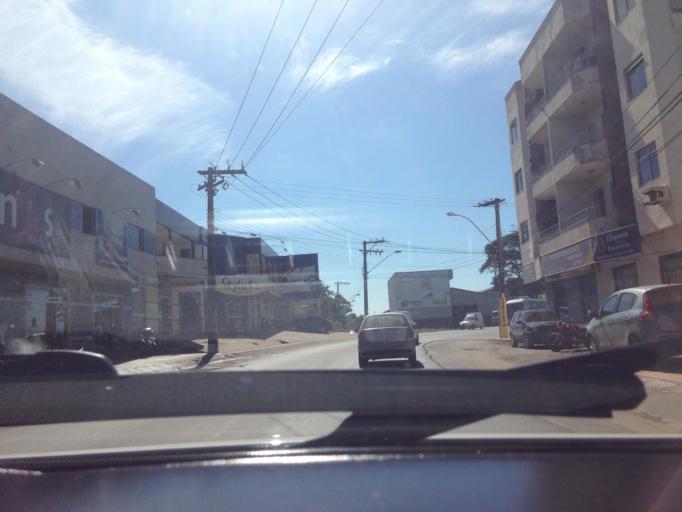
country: BR
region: Espirito Santo
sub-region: Guarapari
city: Guarapari
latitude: -20.6489
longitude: -40.4924
